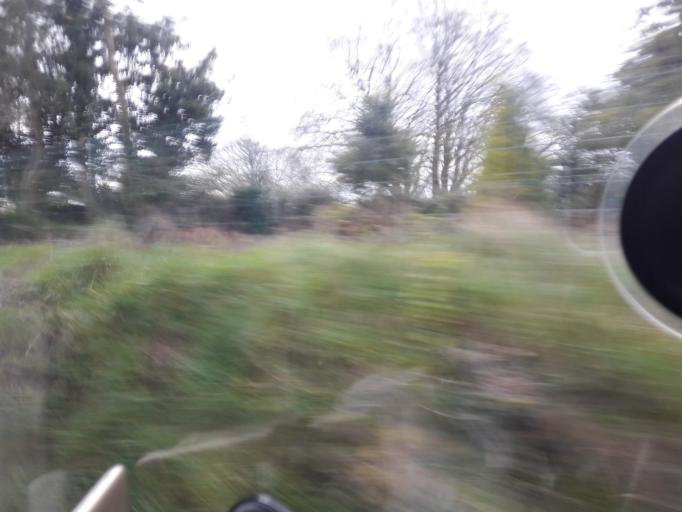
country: IE
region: Leinster
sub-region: An Iarmhi
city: An Muileann gCearr
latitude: 53.6177
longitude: -7.4122
